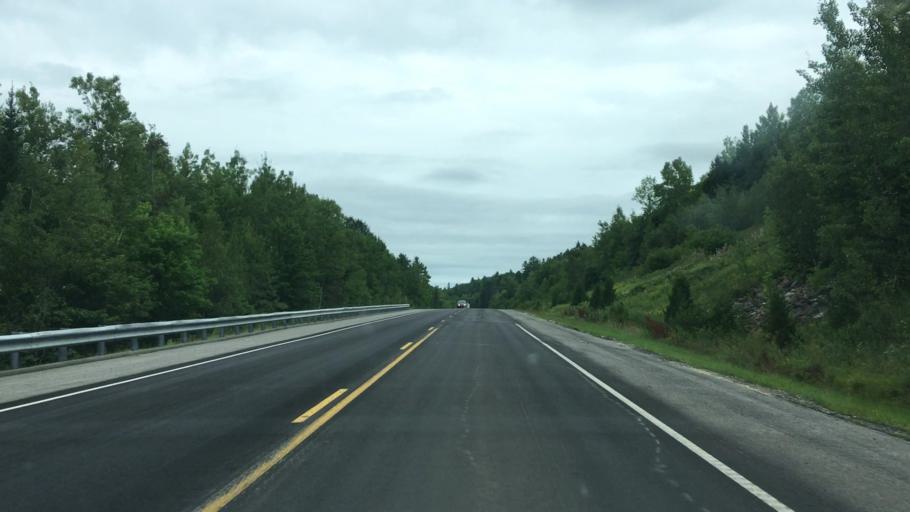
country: US
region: Maine
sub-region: Washington County
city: Cherryfield
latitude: 44.8916
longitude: -67.8562
